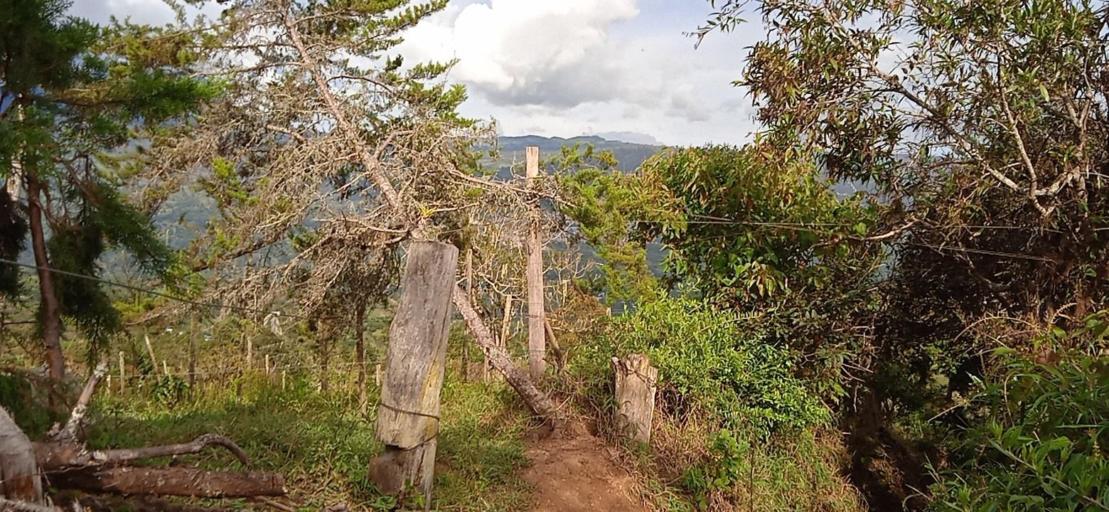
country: CO
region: Cundinamarca
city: Tenza
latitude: 5.0961
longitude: -73.4082
